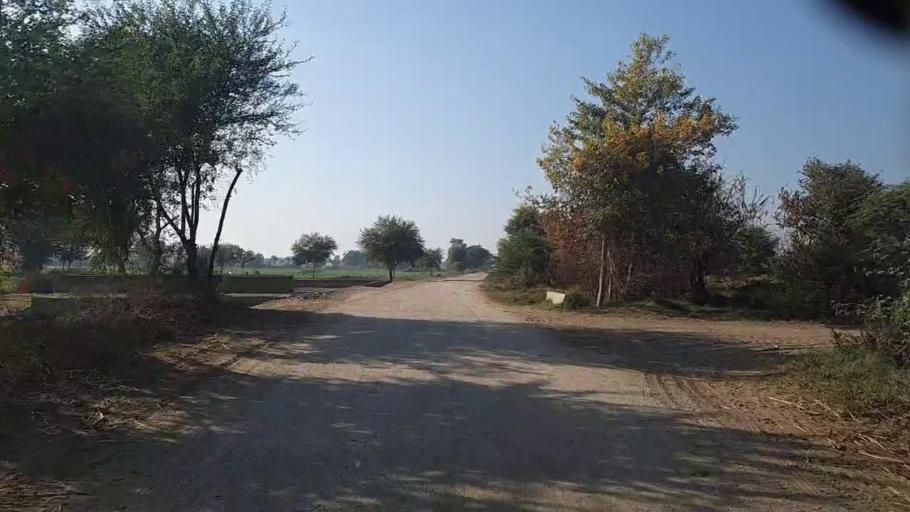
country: PK
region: Sindh
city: Darya Khan Marri
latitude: 26.6812
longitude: 68.3666
